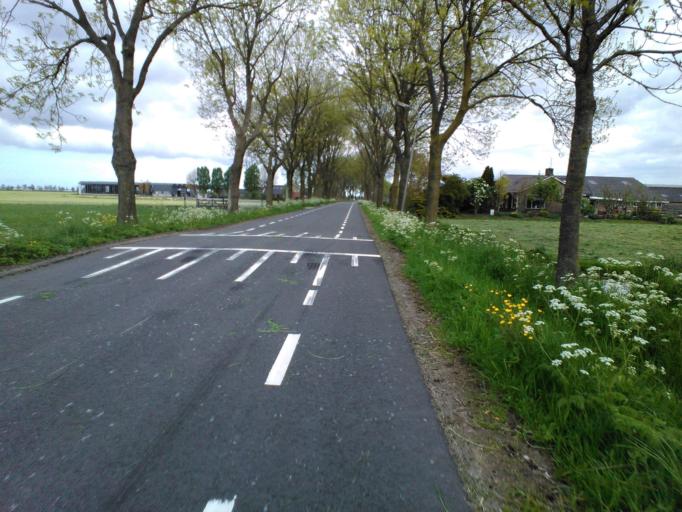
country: NL
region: South Holland
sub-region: Bodegraven-Reeuwijk
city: Bodegraven
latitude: 52.0847
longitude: 4.7233
